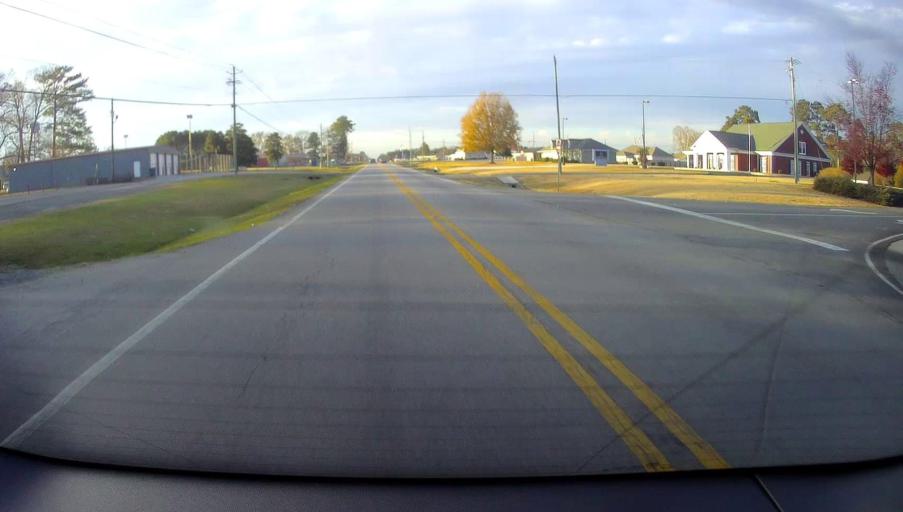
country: US
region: Alabama
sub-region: Blount County
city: Oneonta
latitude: 34.1149
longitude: -86.3877
